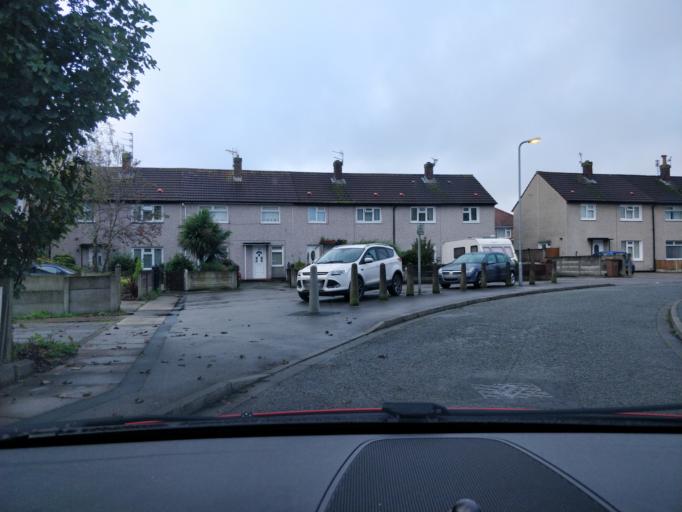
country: GB
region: England
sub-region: Sefton
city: Southport
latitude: 53.6039
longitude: -3.0270
